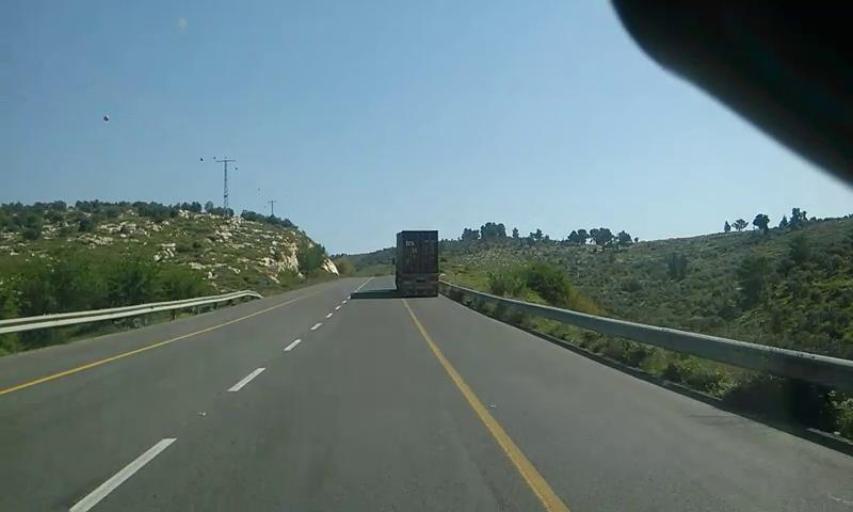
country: PS
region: West Bank
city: Idhna
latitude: 31.5652
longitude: 34.9931
